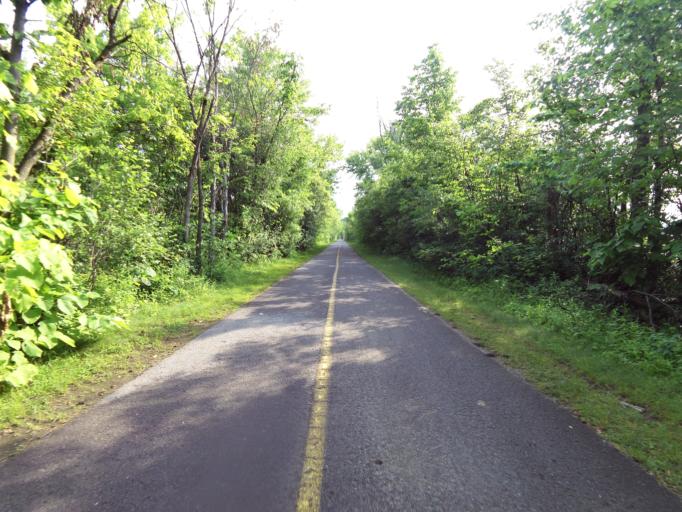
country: CA
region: Ontario
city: Ottawa
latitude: 45.4147
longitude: -75.7599
